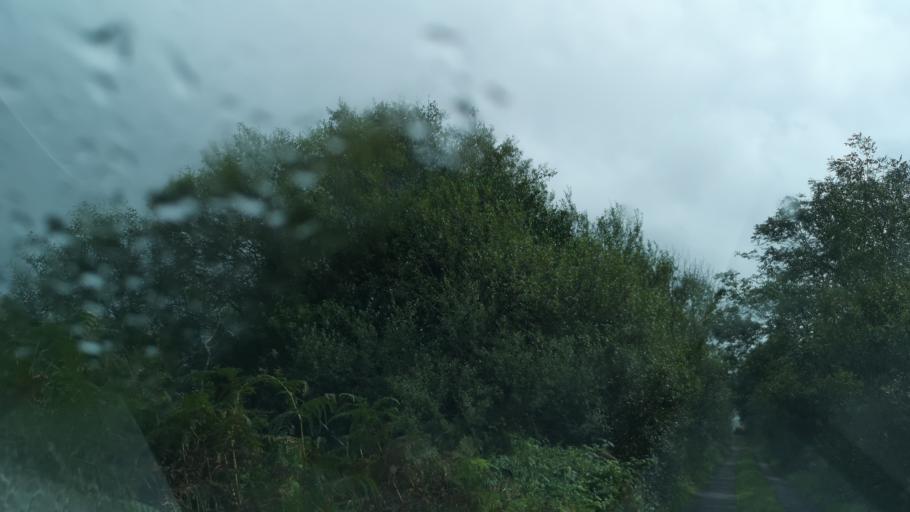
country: IE
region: Connaught
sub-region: County Galway
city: Athenry
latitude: 53.3035
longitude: -8.6299
